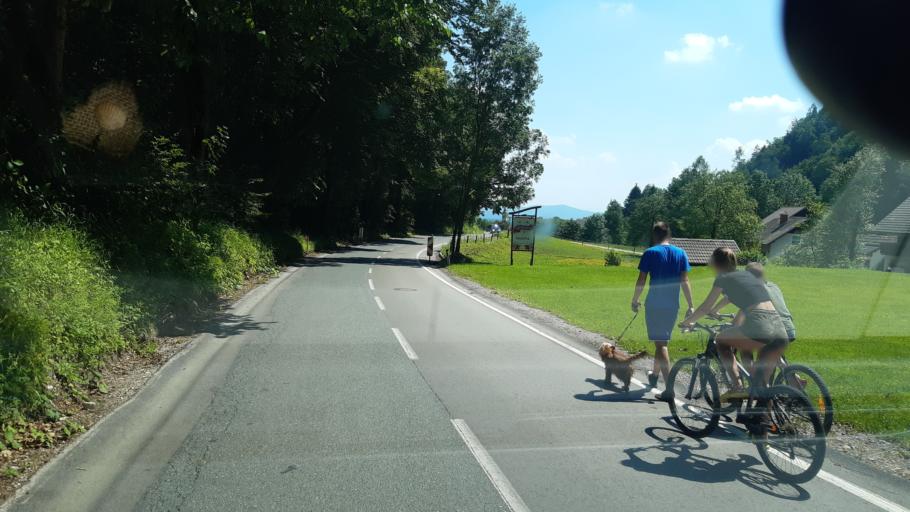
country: SI
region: Cerklje na Gorenjskem
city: Cerklje na Gorenjskem
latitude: 46.2686
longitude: 14.4930
